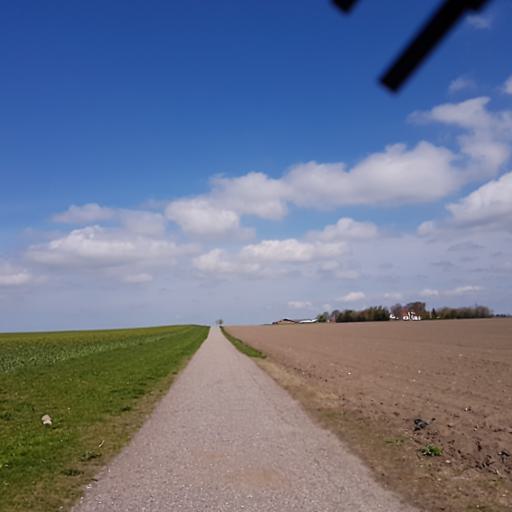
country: DK
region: Capital Region
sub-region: Egedal Kommune
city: Olstykke
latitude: 55.8026
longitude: 12.1499
